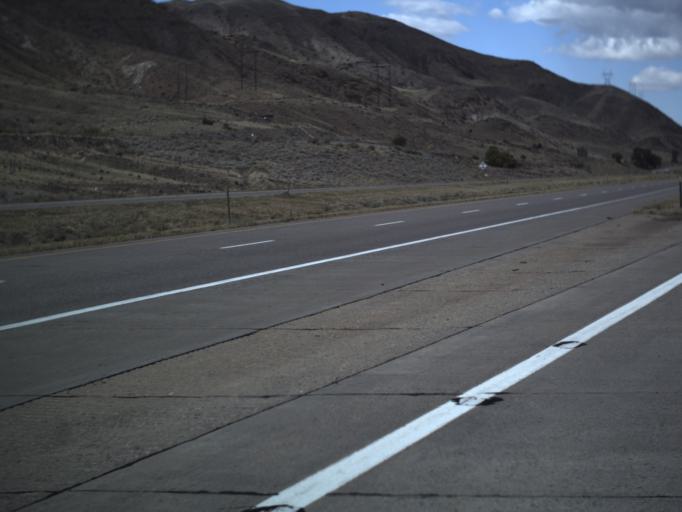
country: US
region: Utah
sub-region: Sevier County
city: Monroe
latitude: 38.6779
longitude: -112.1597
